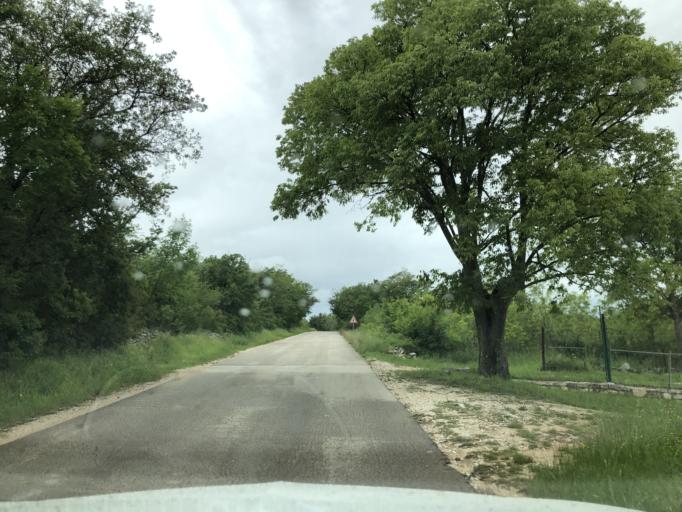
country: HR
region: Istarska
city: Buje
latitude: 45.4364
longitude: 13.6730
